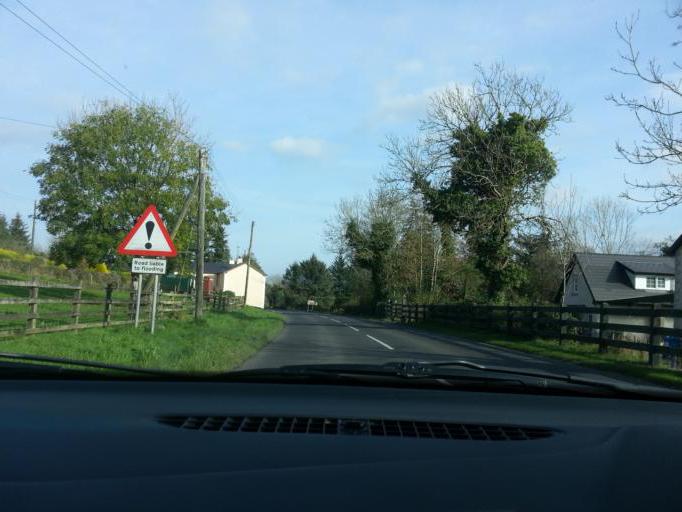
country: IE
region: Ulster
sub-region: County Monaghan
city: Clones
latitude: 54.2303
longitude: -7.2829
